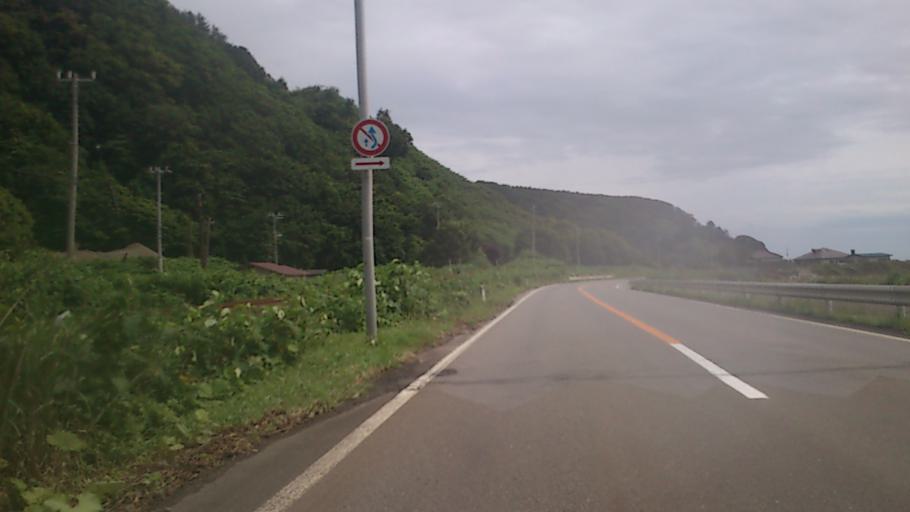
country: JP
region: Akita
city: Noshiromachi
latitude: 40.4546
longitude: 139.9426
